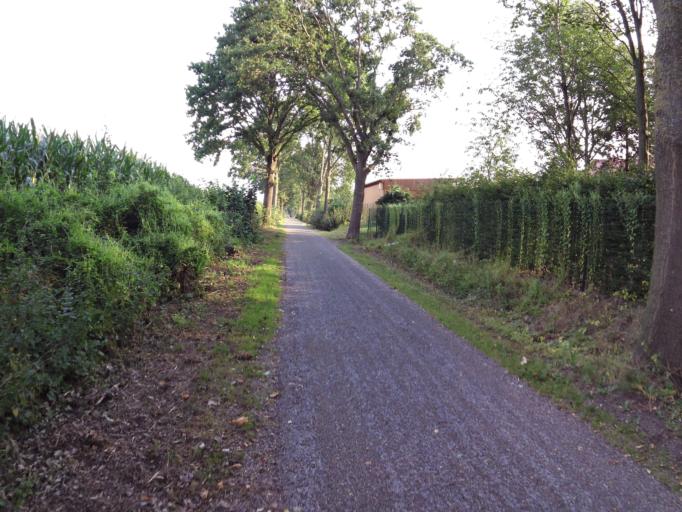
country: DE
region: North Rhine-Westphalia
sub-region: Regierungsbezirk Detmold
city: Petershagen
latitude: 52.4029
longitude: 8.9643
